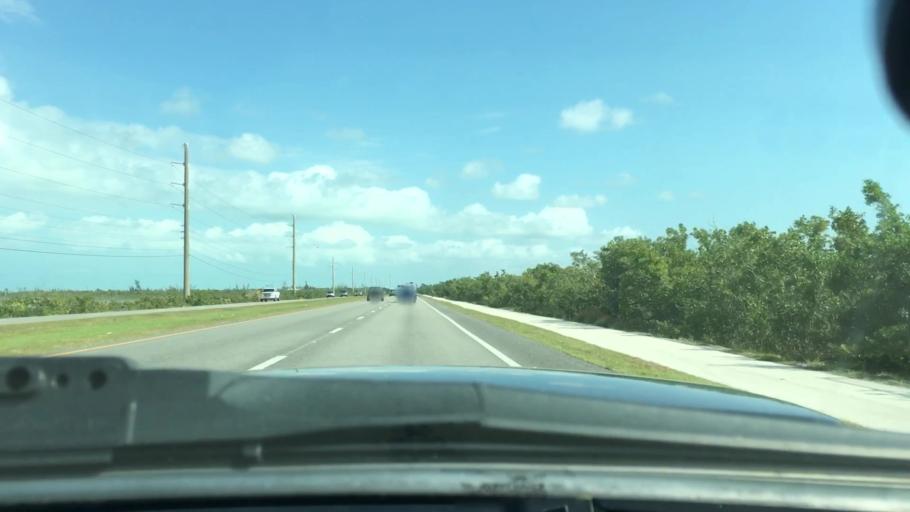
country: US
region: Florida
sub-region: Monroe County
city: Stock Island
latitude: 24.5809
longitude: -81.7051
